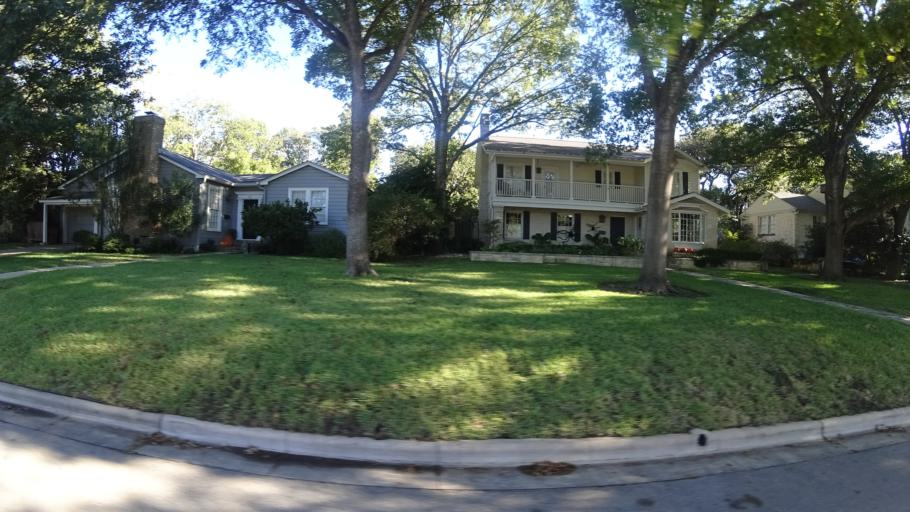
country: US
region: Texas
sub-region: Travis County
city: Rollingwood
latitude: 30.2986
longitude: -97.7735
